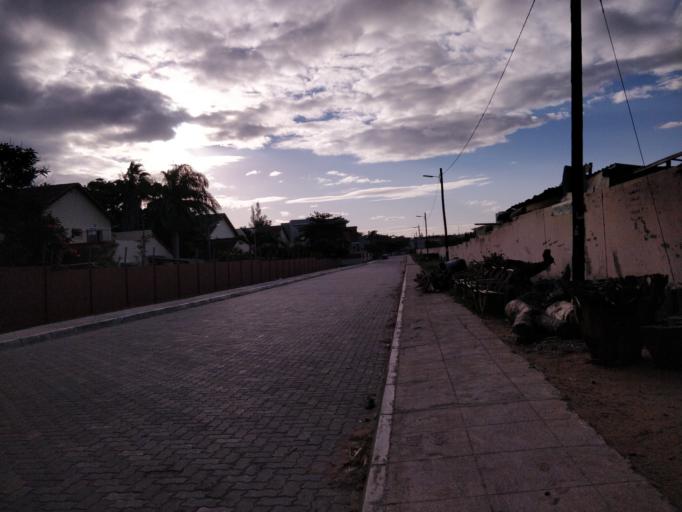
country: MZ
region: Maputo City
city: Maputo
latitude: -25.9470
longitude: 32.6181
